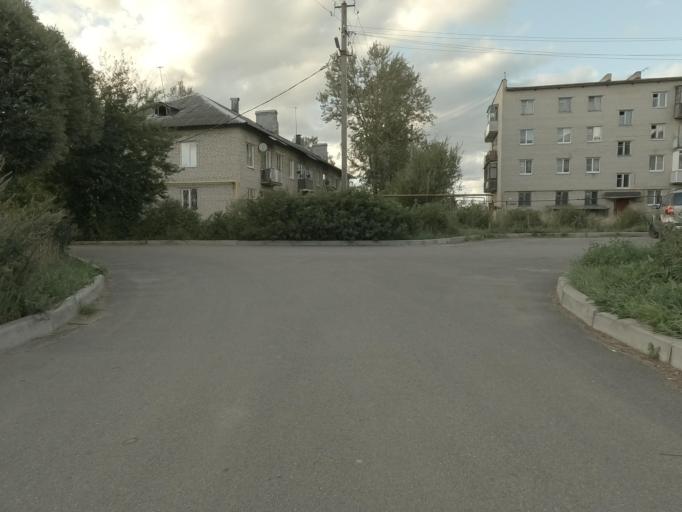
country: RU
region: Leningrad
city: Mga
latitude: 59.7522
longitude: 31.0386
